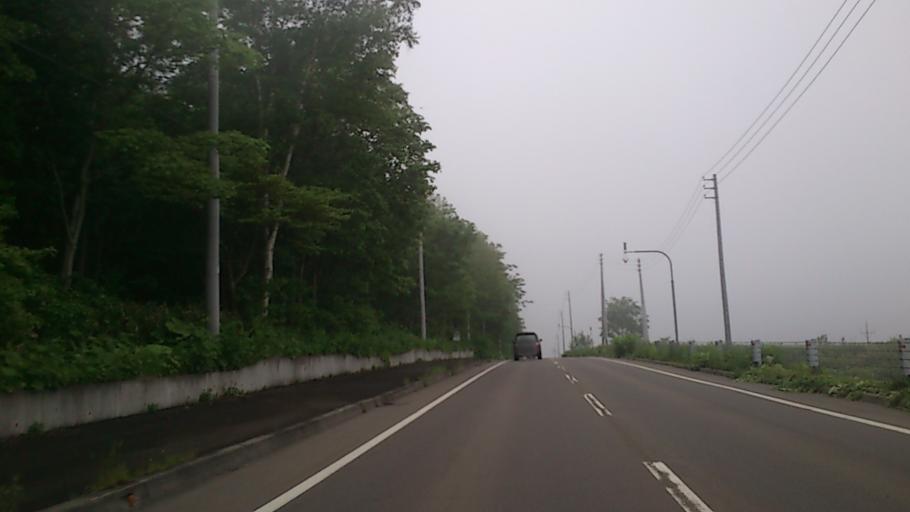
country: JP
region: Hokkaido
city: Niseko Town
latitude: 42.8808
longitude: 140.8114
